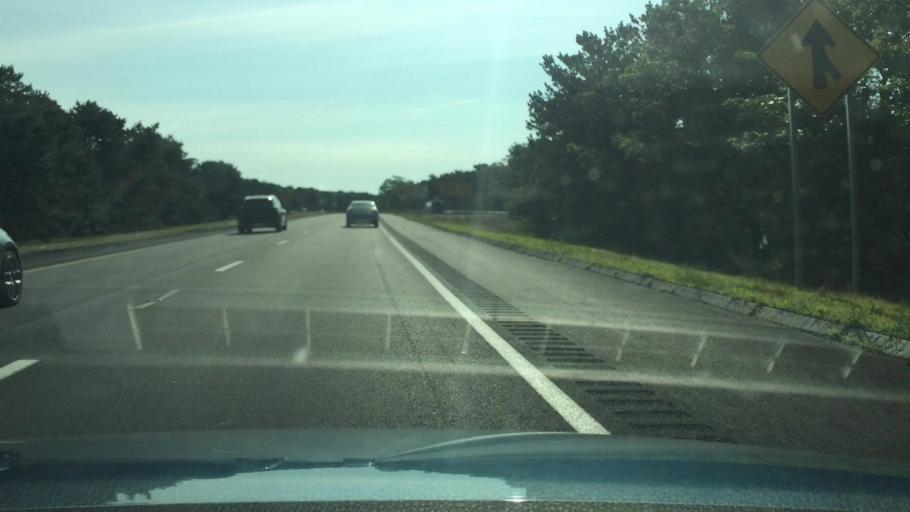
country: US
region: Massachusetts
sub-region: Barnstable County
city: South Dennis
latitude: 41.6988
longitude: -70.1500
